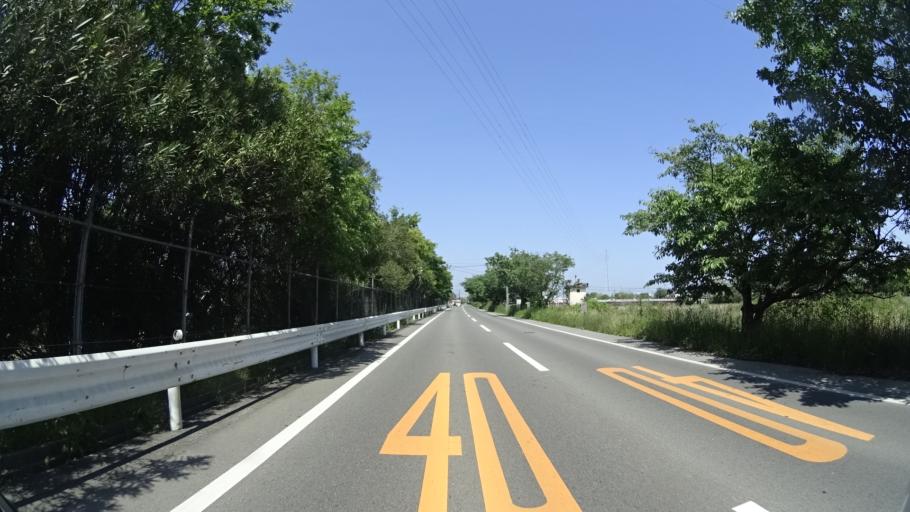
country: JP
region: Ehime
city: Hojo
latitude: 34.0485
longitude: 132.9872
